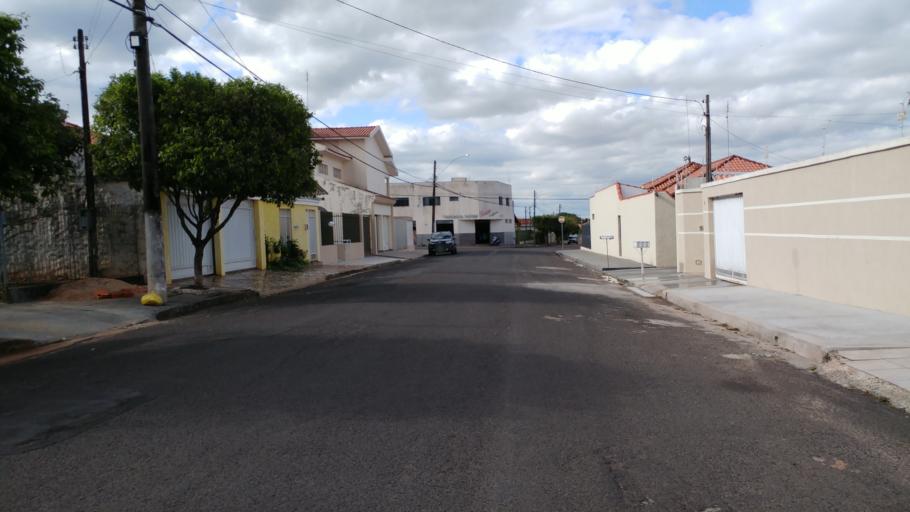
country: BR
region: Sao Paulo
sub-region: Paraguacu Paulista
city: Paraguacu Paulista
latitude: -22.4087
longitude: -50.5774
